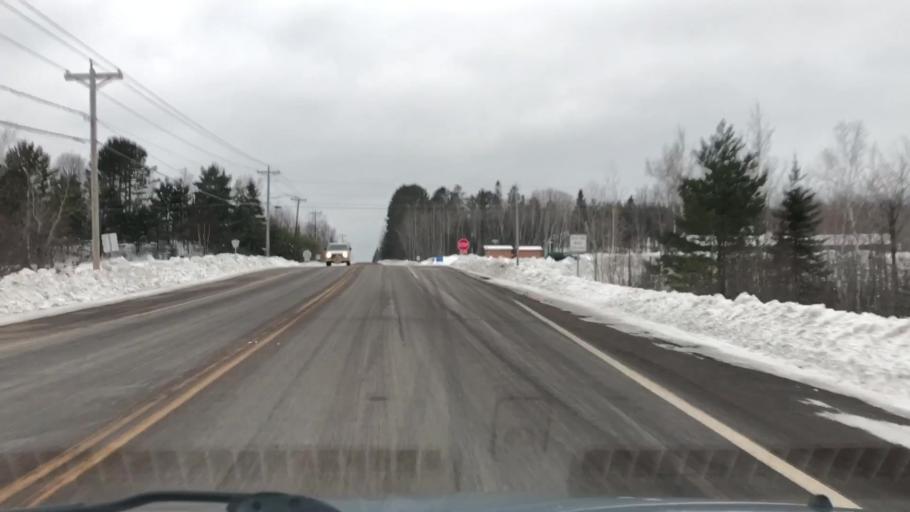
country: US
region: Minnesota
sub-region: Saint Louis County
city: Arnold
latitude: 46.8645
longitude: -92.1111
